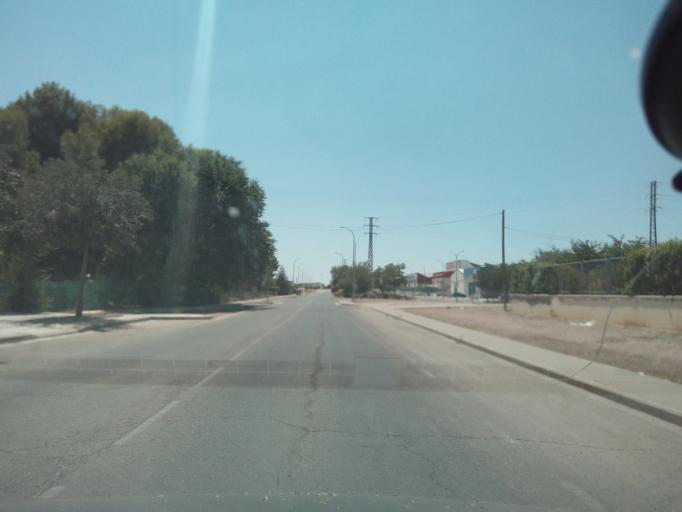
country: ES
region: Castille-La Mancha
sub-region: Province of Toledo
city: Villacanas
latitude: 39.6133
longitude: -3.3431
